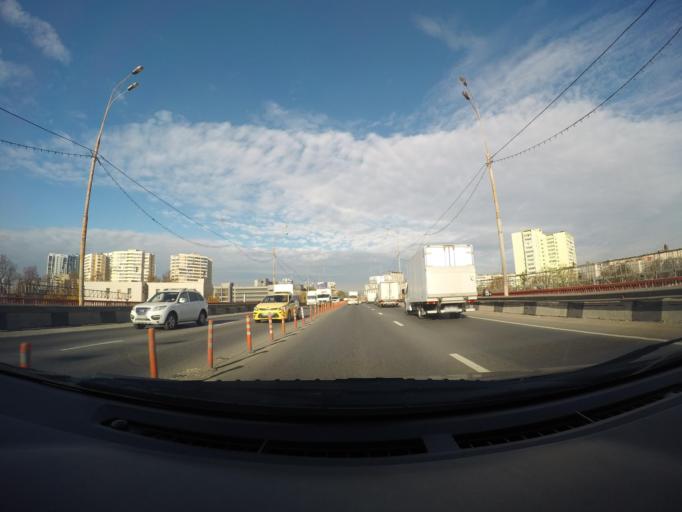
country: RU
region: Moskovskaya
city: Mytishchi
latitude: 55.9185
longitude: 37.7667
